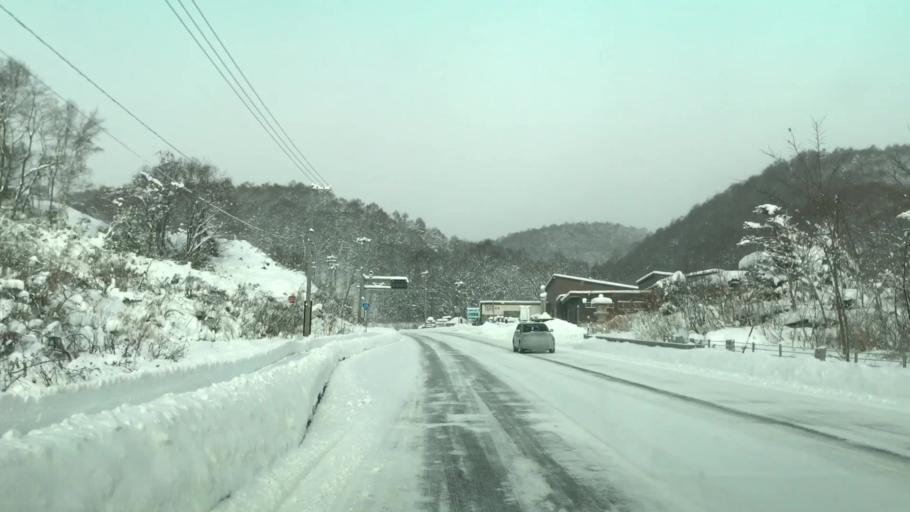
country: JP
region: Hokkaido
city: Yoichi
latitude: 43.2180
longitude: 140.7422
